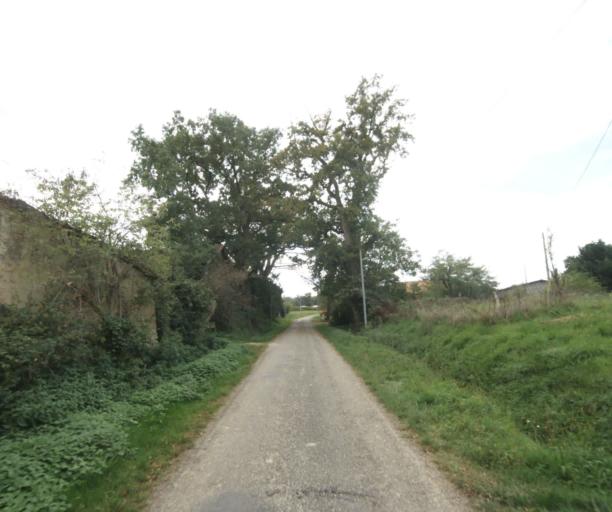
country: FR
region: Midi-Pyrenees
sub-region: Departement du Gers
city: Montreal
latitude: 43.9271
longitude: 0.1374
